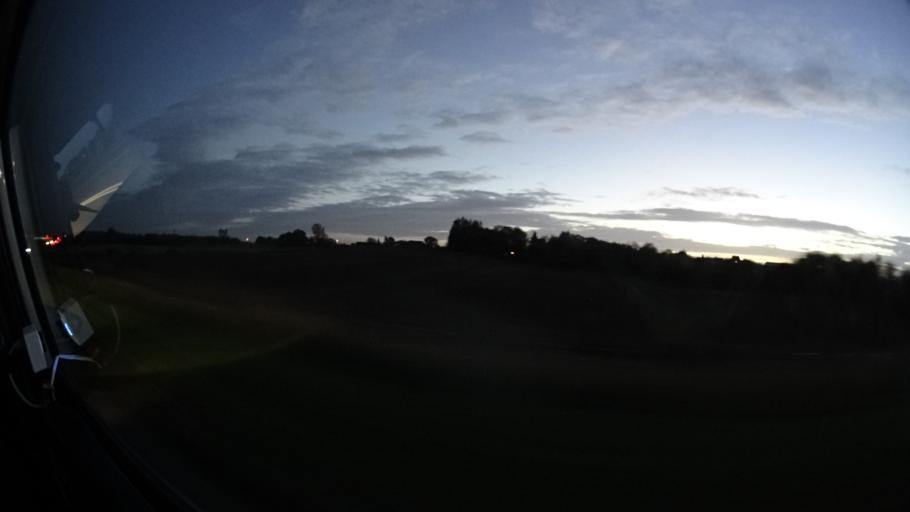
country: DK
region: South Denmark
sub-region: Odense Kommune
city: Hojby
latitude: 55.3284
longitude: 10.4389
